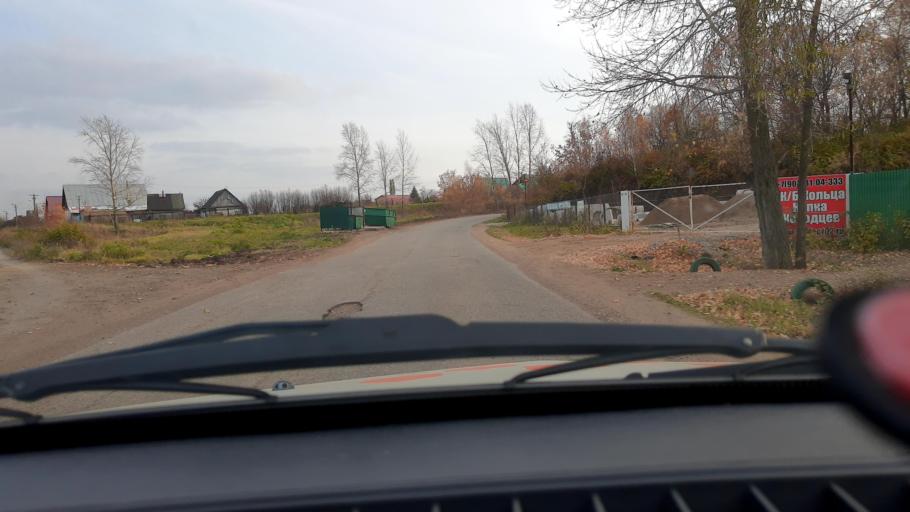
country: RU
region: Bashkortostan
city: Iglino
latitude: 54.7984
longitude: 56.3138
